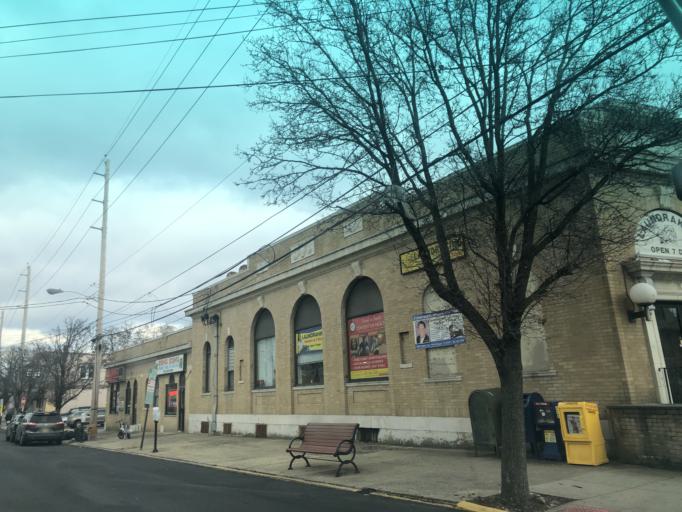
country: US
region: New Jersey
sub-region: Hudson County
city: Union City
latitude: 40.7827
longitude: -74.0333
